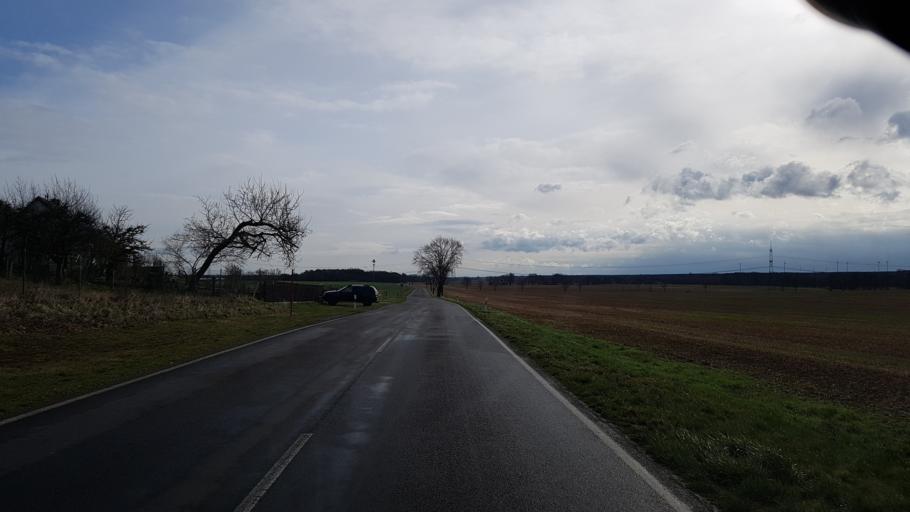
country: DE
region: Brandenburg
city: Schlieben
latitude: 51.7175
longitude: 13.3890
